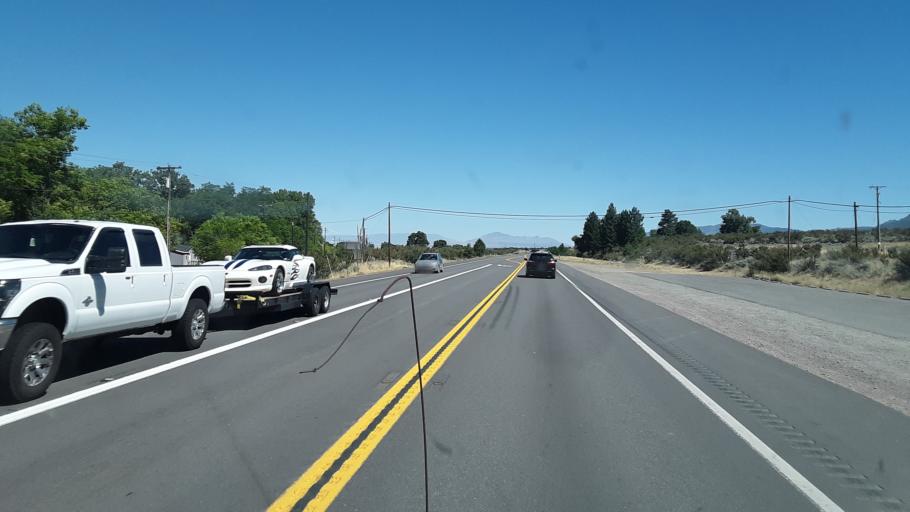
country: US
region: California
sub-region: Lassen County
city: Janesville
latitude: 40.2903
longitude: -120.5012
